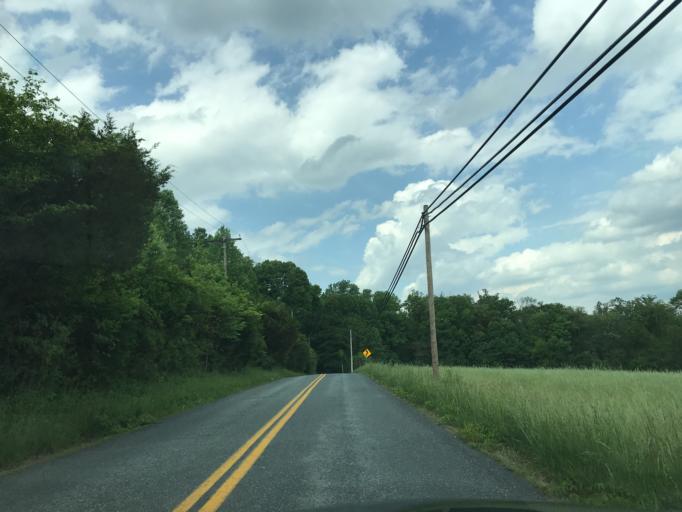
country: US
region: Pennsylvania
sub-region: York County
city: Susquehanna Trails
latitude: 39.6981
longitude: -76.3384
